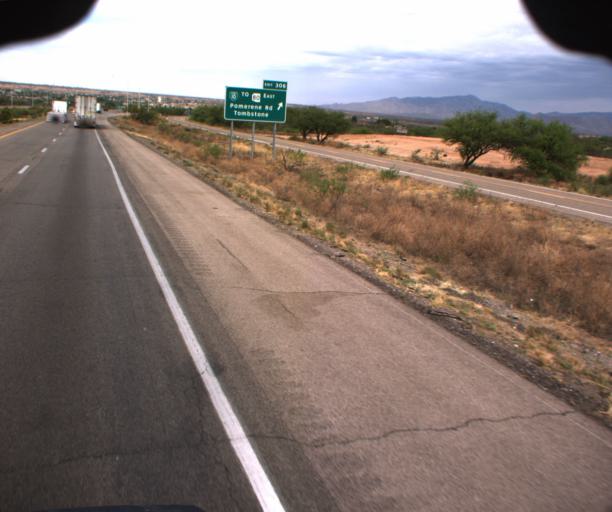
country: US
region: Arizona
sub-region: Cochise County
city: Benson
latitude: 31.9655
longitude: -110.2643
